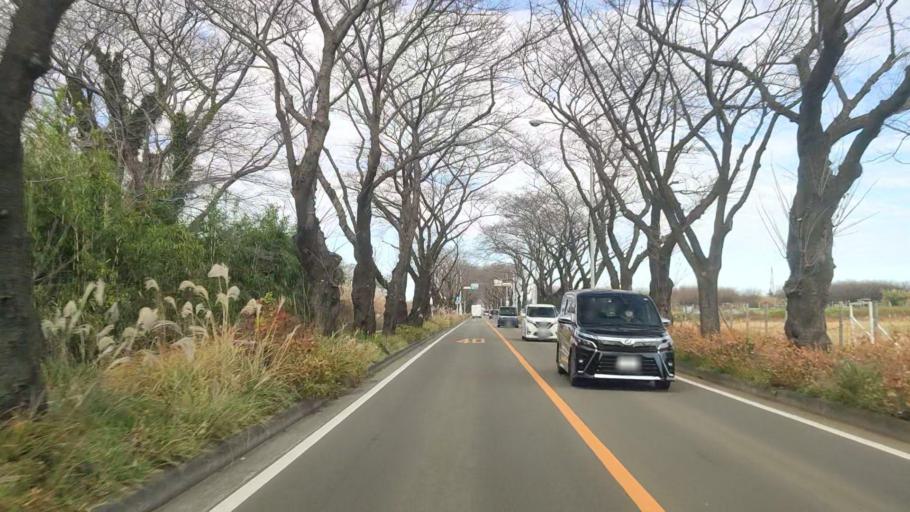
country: JP
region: Kanagawa
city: Minami-rinkan
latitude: 35.4884
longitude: 139.4803
